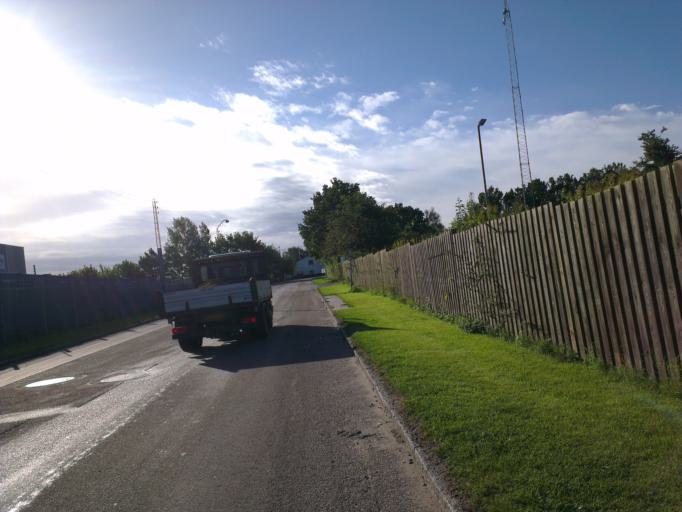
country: DK
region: Capital Region
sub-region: Frederikssund Kommune
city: Frederikssund
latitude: 55.8469
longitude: 12.0758
